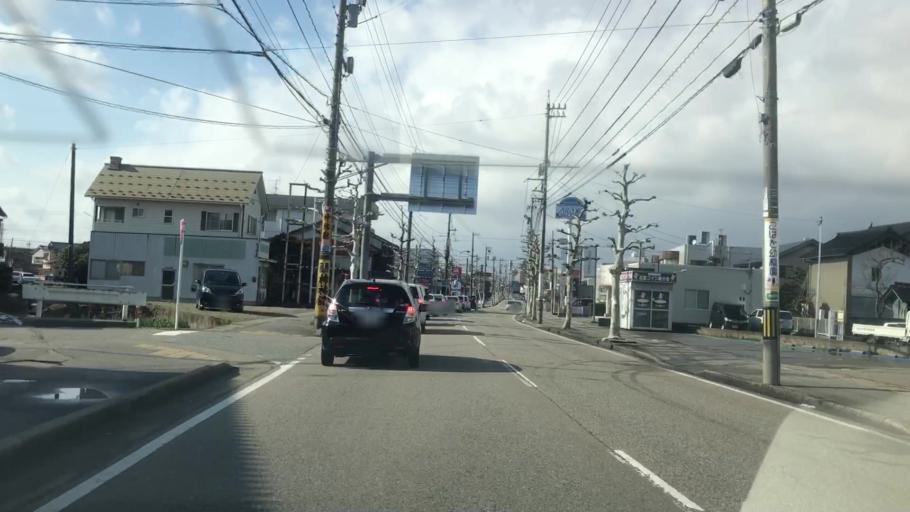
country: JP
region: Toyama
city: Takaoka
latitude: 36.7374
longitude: 137.0306
